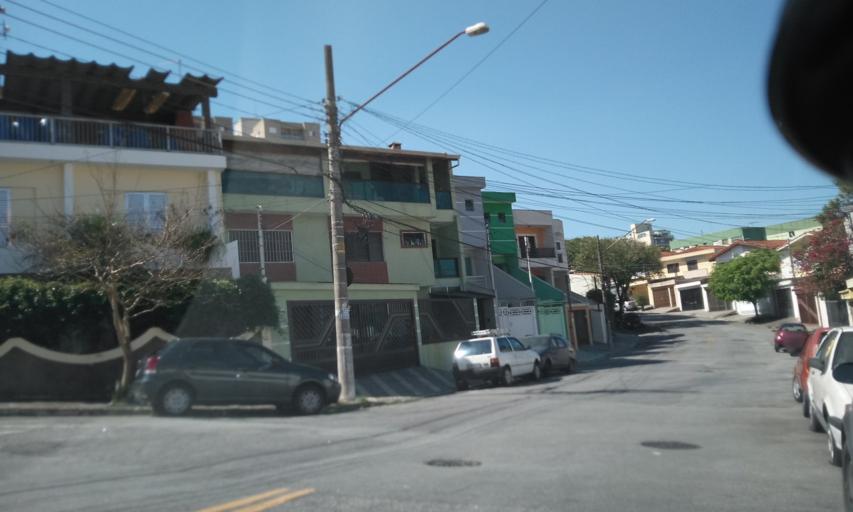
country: BR
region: Sao Paulo
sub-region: Sao Bernardo Do Campo
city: Sao Bernardo do Campo
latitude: -23.7222
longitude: -46.5711
